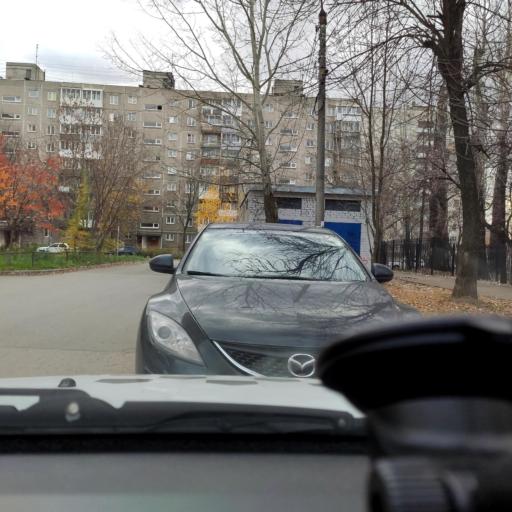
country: RU
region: Perm
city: Perm
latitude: 58.0121
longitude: 56.2213
